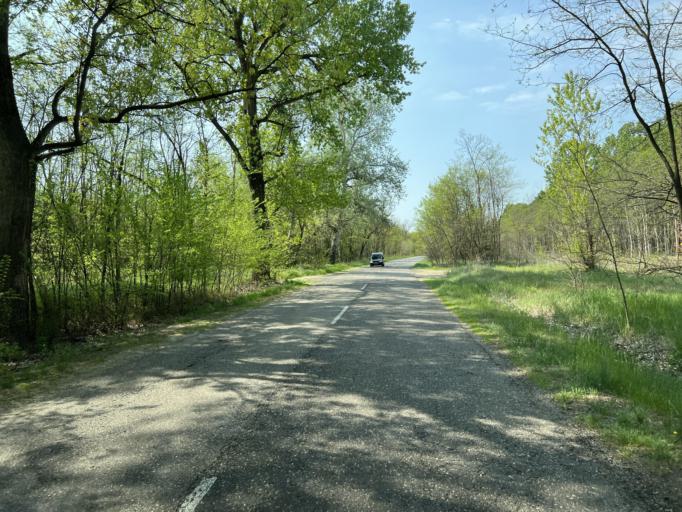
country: HU
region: Pest
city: Tortel
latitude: 47.0792
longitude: 19.8723
